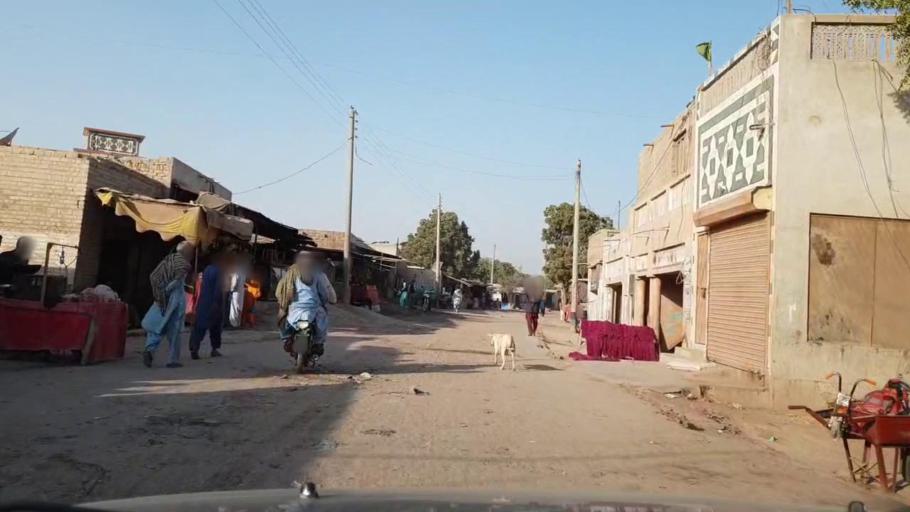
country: PK
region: Sindh
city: Chambar
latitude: 25.2172
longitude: 68.7796
